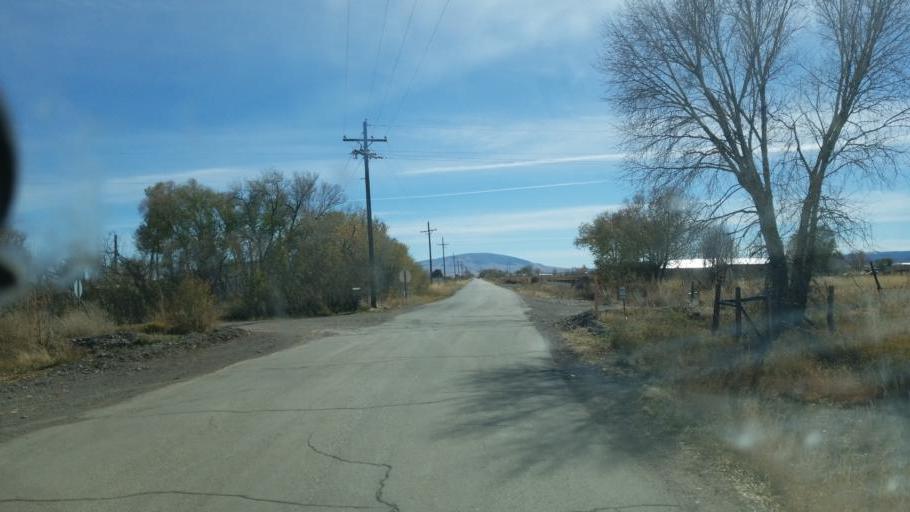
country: US
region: Colorado
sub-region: Conejos County
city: Conejos
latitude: 37.0867
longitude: -106.0194
